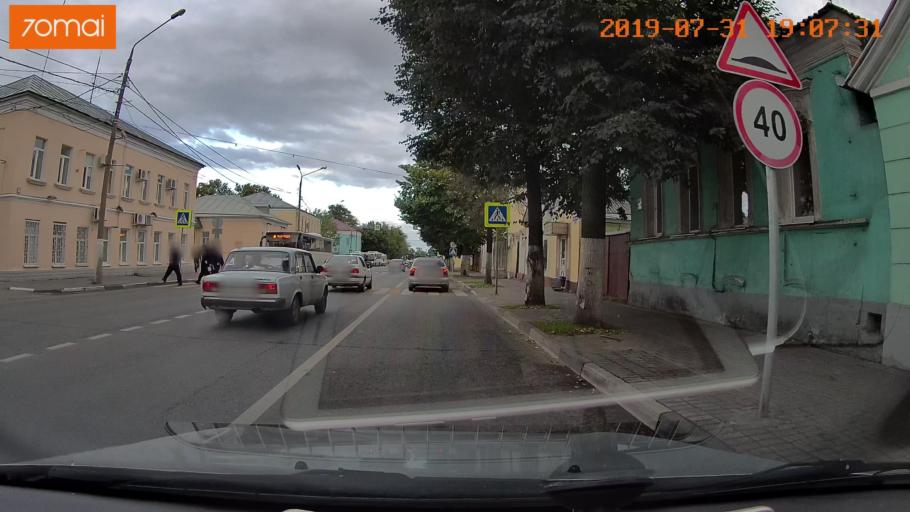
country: RU
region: Moskovskaya
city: Kolomna
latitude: 55.0980
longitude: 38.7610
